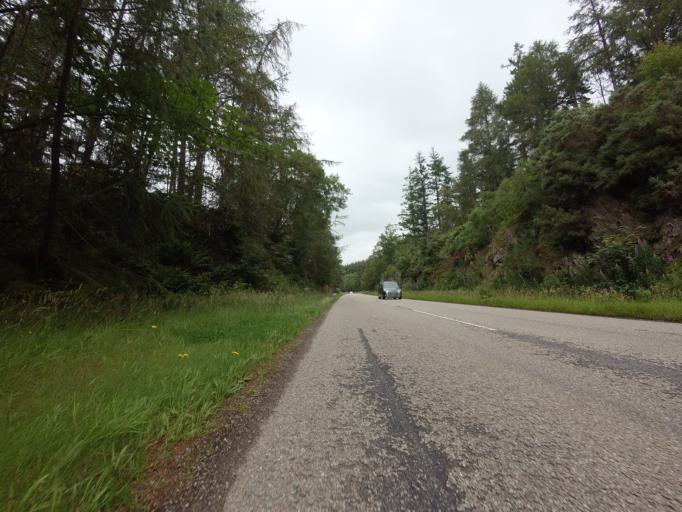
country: GB
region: Scotland
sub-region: Highland
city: Alness
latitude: 57.9053
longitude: -4.3599
